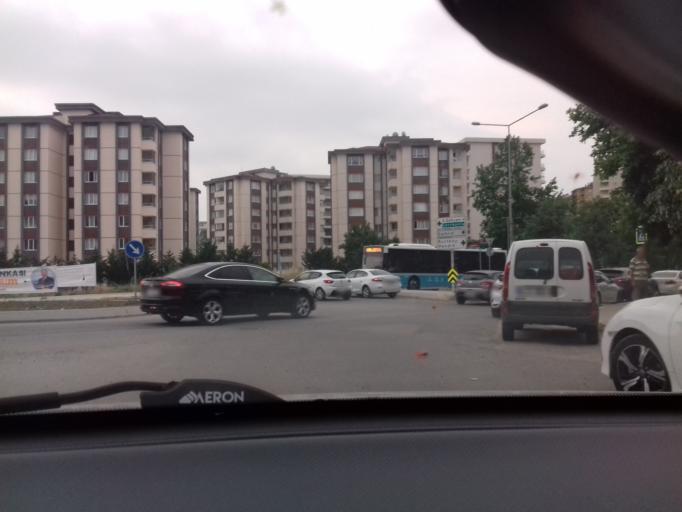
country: TR
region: Istanbul
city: Sultanbeyli
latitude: 40.9310
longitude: 29.2973
